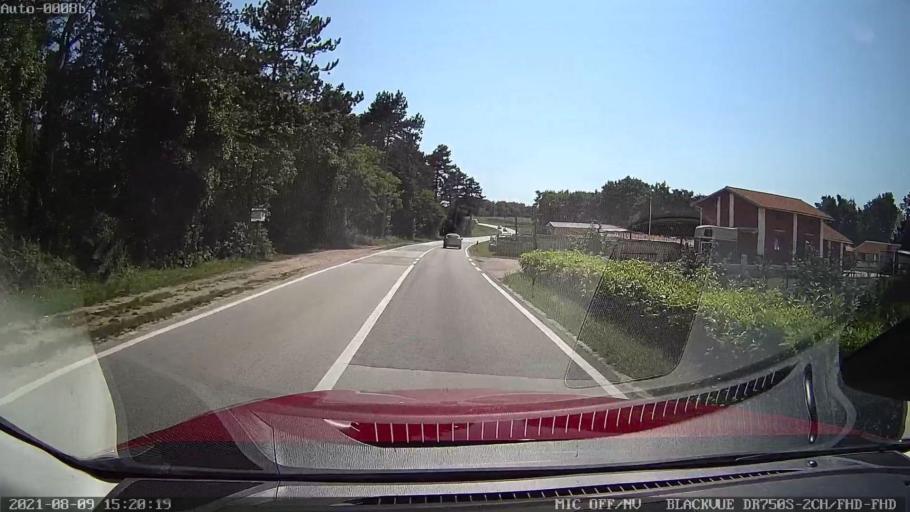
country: HR
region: Istarska
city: Pazin
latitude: 45.2075
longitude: 13.8993
